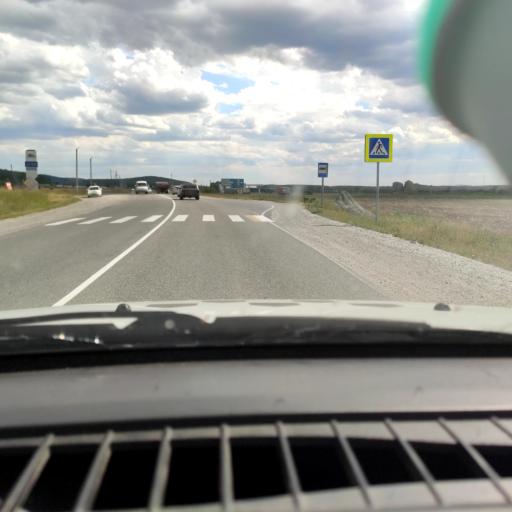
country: RU
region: Chelyabinsk
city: Miass
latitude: 54.9415
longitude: 60.0495
